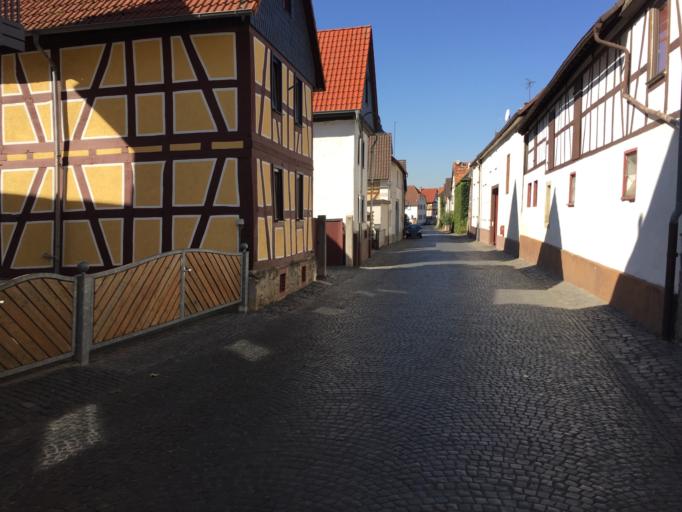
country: DE
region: Hesse
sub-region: Regierungsbezirk Darmstadt
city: Nidda
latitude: 50.4266
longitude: 8.9424
